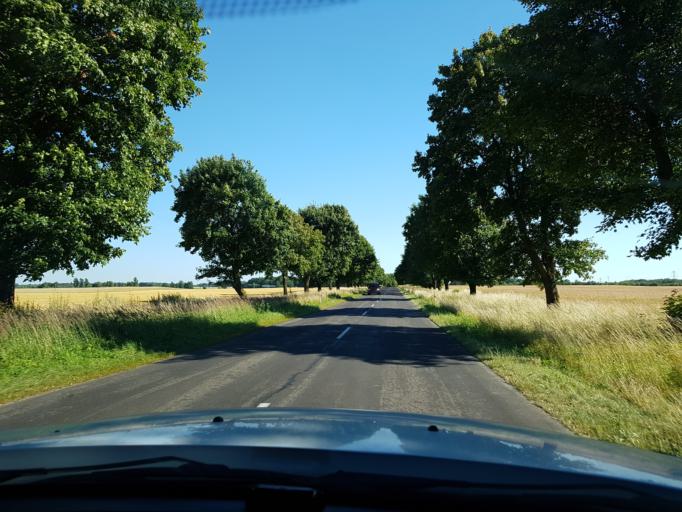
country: PL
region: West Pomeranian Voivodeship
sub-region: Powiat lobeski
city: Lobez
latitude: 53.6918
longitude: 15.6070
